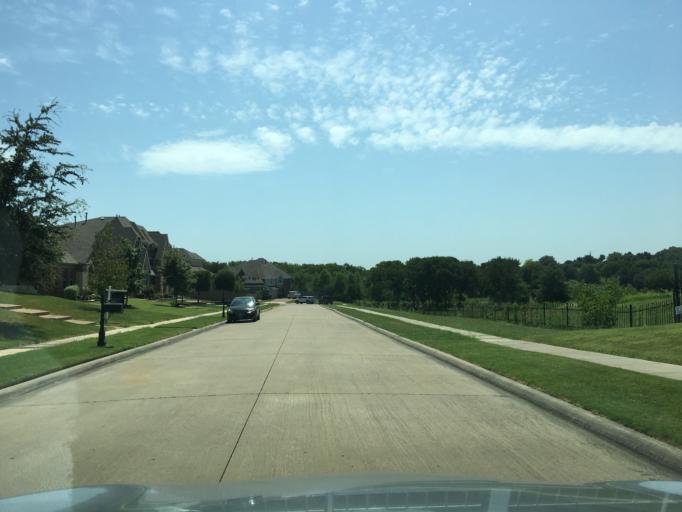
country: US
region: Texas
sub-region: Dallas County
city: Rowlett
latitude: 32.8863
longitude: -96.6011
